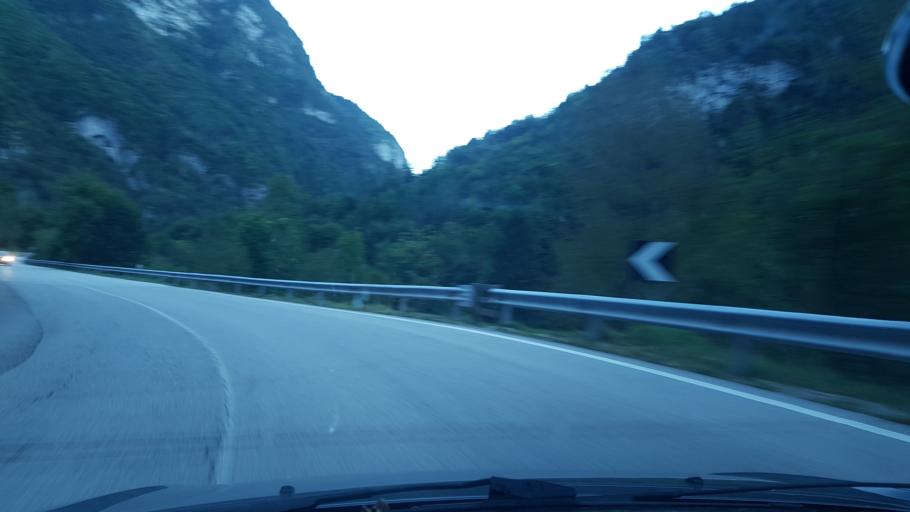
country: IT
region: Veneto
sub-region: Provincia di Belluno
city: Longarone
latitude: 46.2972
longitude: 12.2326
